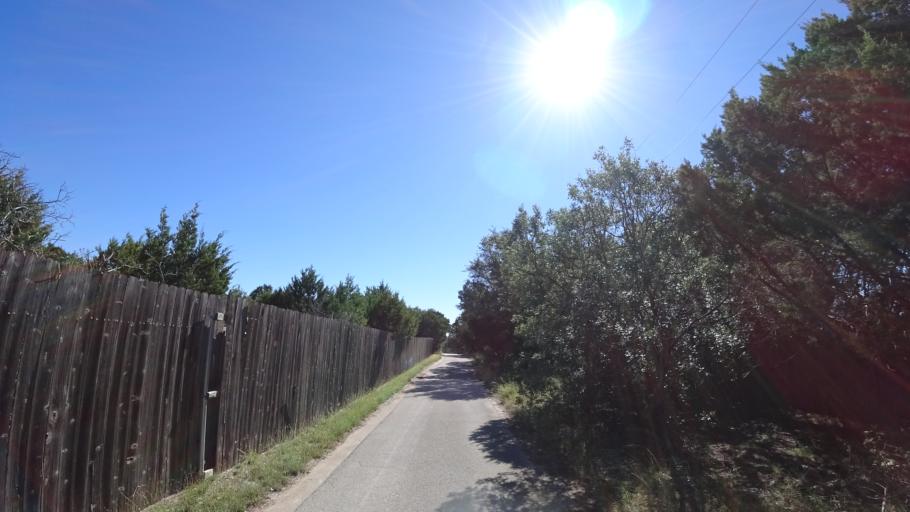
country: US
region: Texas
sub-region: Travis County
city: West Lake Hills
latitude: 30.3240
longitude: -97.7991
